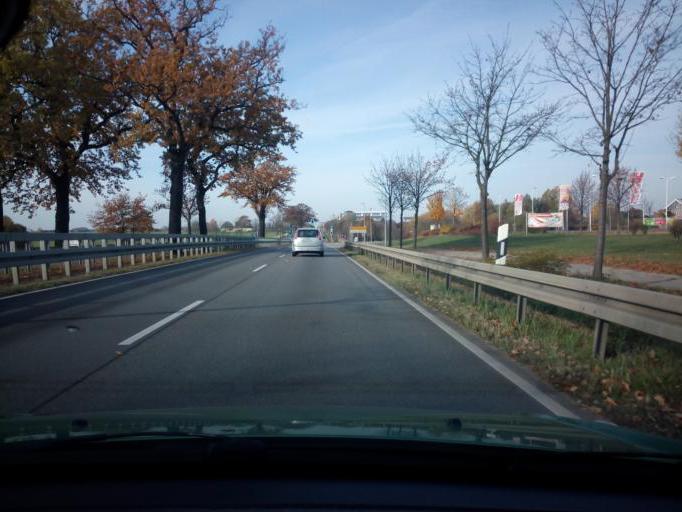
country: DE
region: Berlin
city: Mahlsdorf
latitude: 52.5027
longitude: 13.6344
